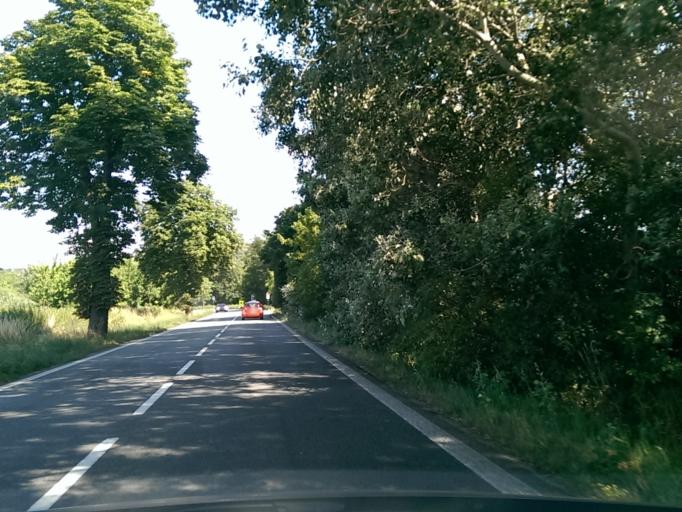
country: CZ
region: South Moravian
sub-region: Okres Breclav
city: Mikulov
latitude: 48.7916
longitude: 16.6718
